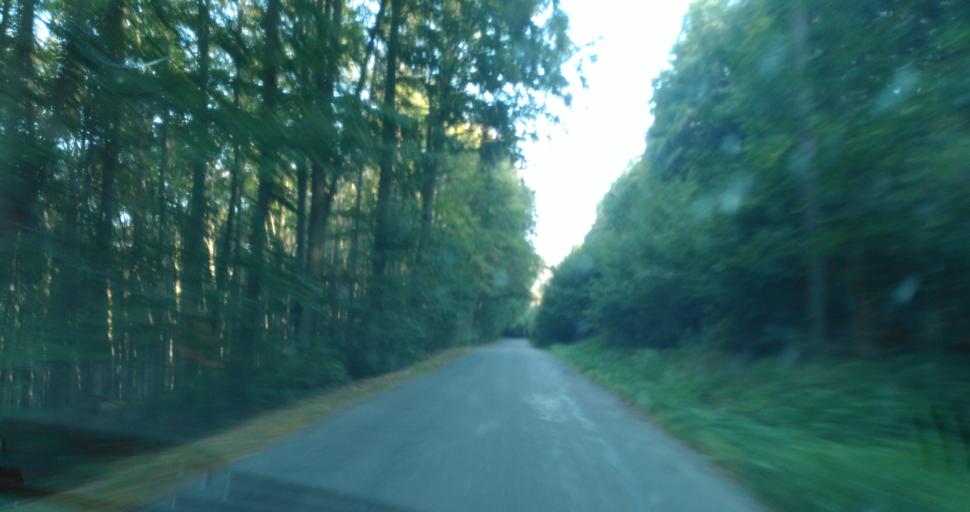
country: CZ
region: Central Bohemia
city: Roztoky
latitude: 50.0016
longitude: 13.8581
